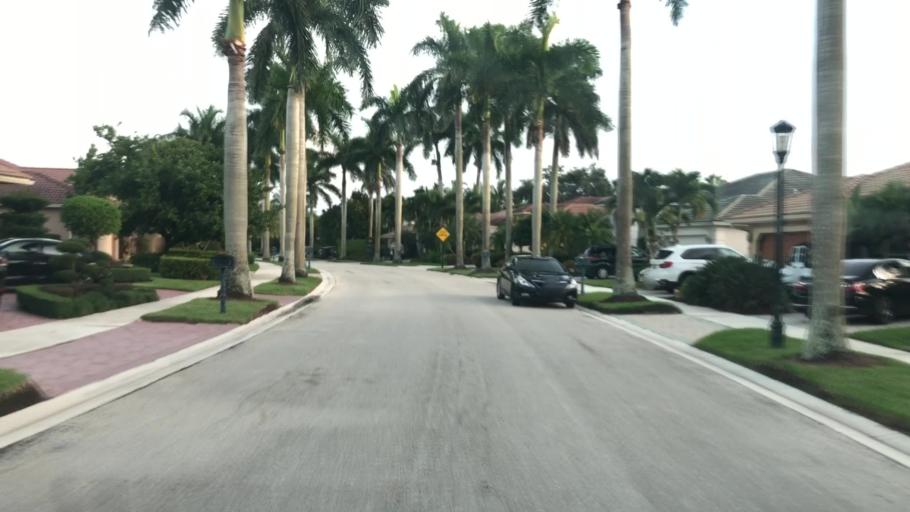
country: US
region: Florida
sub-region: Broward County
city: Weston
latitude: 26.0993
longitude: -80.4014
